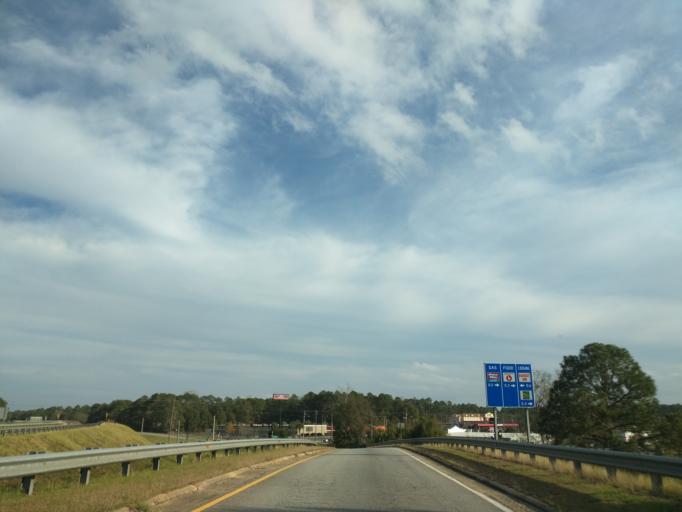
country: US
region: Georgia
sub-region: Decatur County
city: Bainbridge
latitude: 30.8906
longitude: -84.5683
